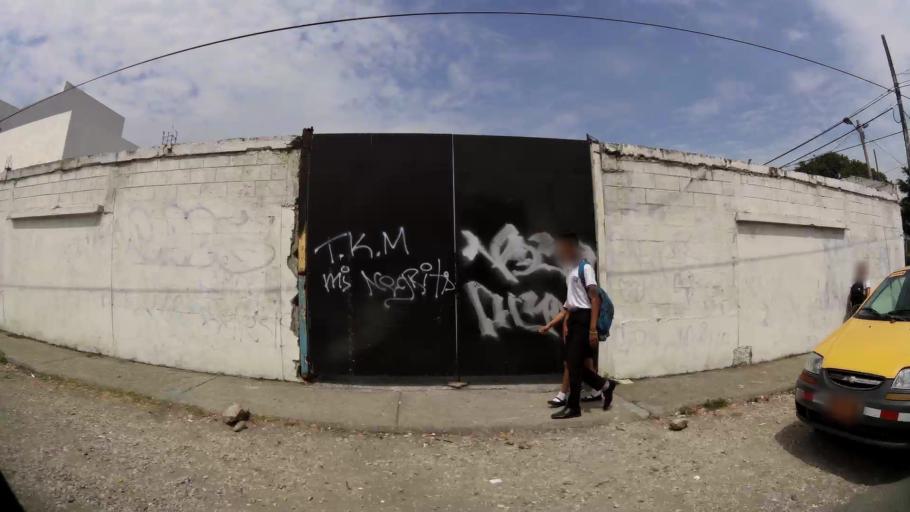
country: EC
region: Guayas
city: Eloy Alfaro
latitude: -2.1433
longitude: -79.8999
